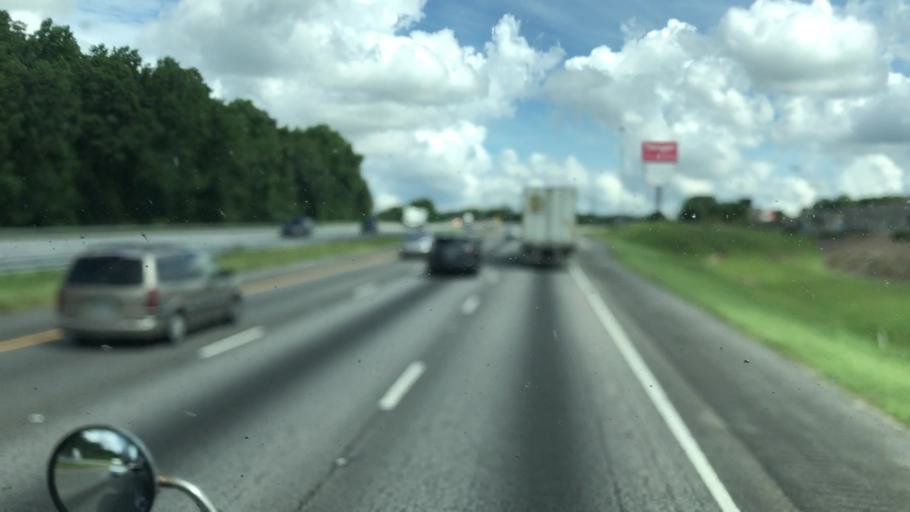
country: US
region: Georgia
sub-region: Henry County
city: Locust Grove
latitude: 33.3477
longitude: -84.1239
